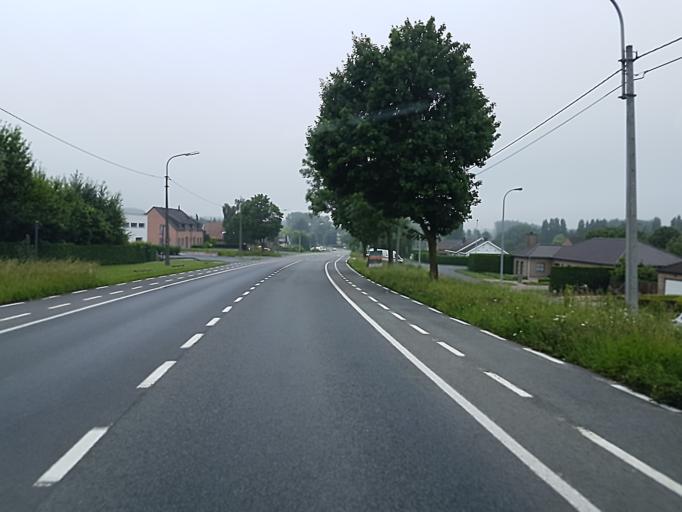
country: BE
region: Flanders
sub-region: Provincie West-Vlaanderen
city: Kortrijk
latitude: 50.7914
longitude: 3.2387
